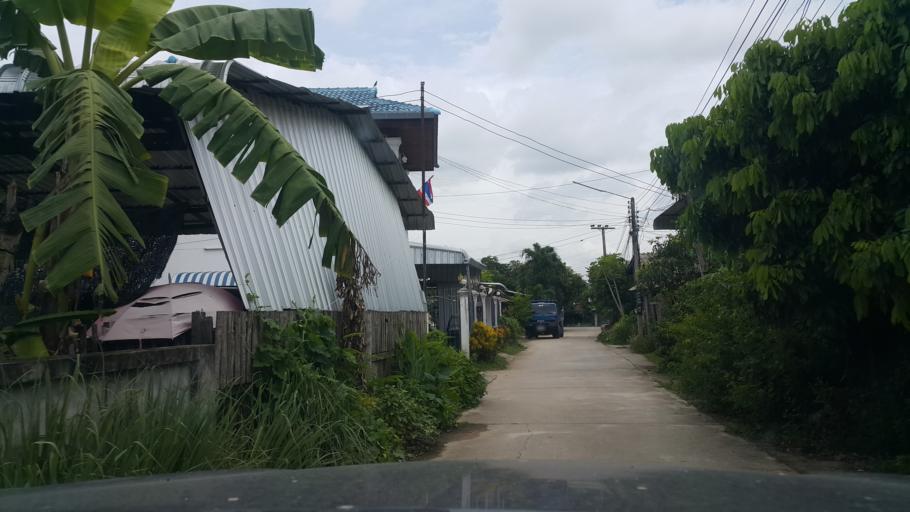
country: TH
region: Lamphun
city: Ban Thi
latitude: 18.6437
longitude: 99.1440
